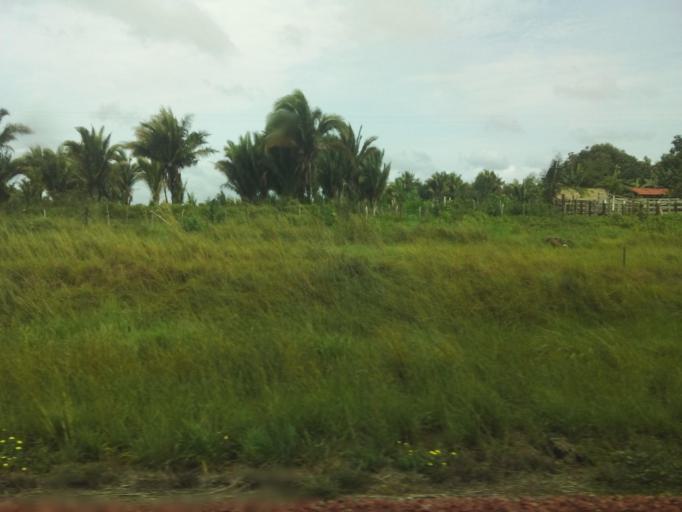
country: BR
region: Maranhao
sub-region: Arari
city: Arari
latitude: -3.5165
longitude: -44.6279
